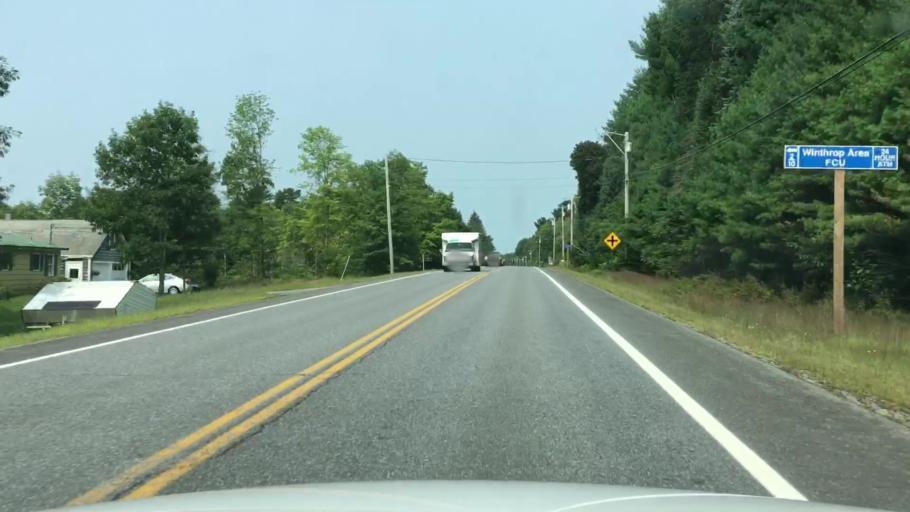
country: US
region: Maine
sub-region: Kennebec County
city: Wayne
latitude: 44.3432
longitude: -70.0307
